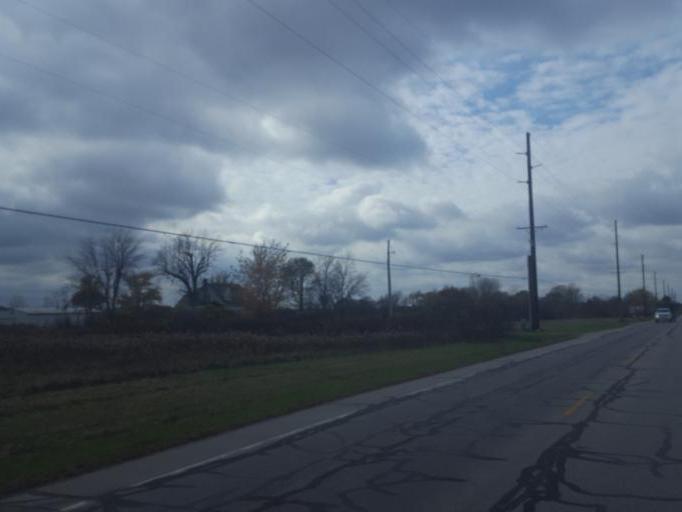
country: US
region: Ohio
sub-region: Crawford County
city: Crestline
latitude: 40.7867
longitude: -82.7056
